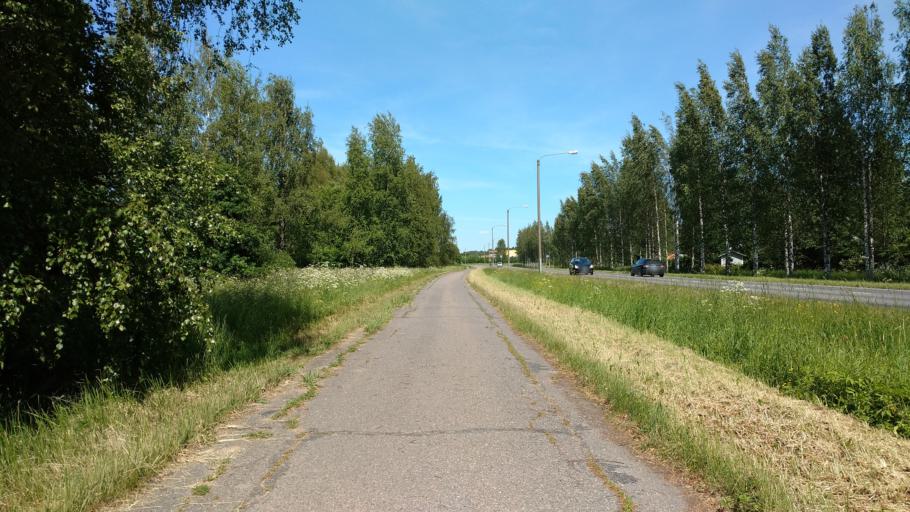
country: FI
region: Varsinais-Suomi
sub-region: Salo
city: Salo
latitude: 60.3944
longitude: 23.1505
